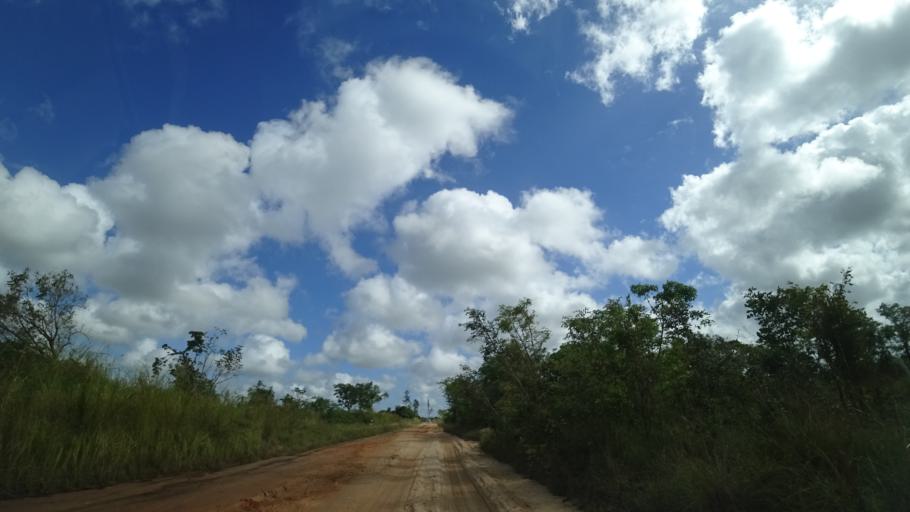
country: MZ
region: Sofala
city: Dondo
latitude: -19.4318
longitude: 34.7104
